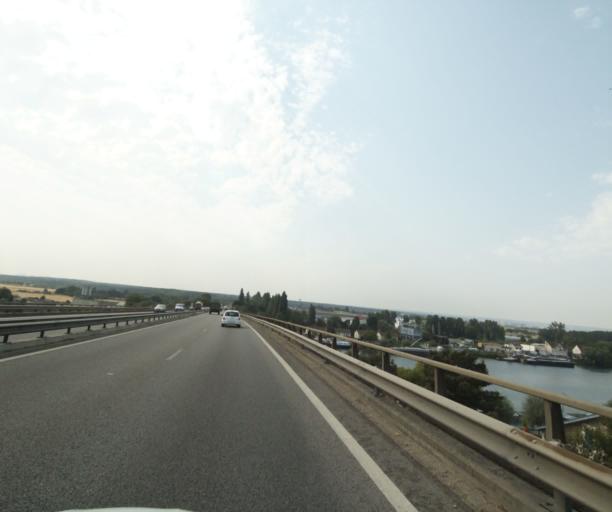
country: FR
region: Ile-de-France
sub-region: Departement des Yvelines
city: Conflans-Sainte-Honorine
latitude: 48.9901
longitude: 2.0817
